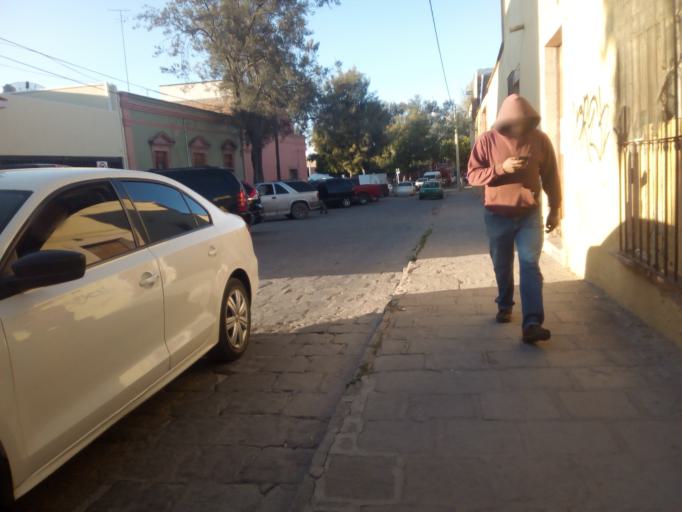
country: MX
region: Guerrero
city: San Luis de la Paz
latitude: 21.2965
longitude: -100.5165
